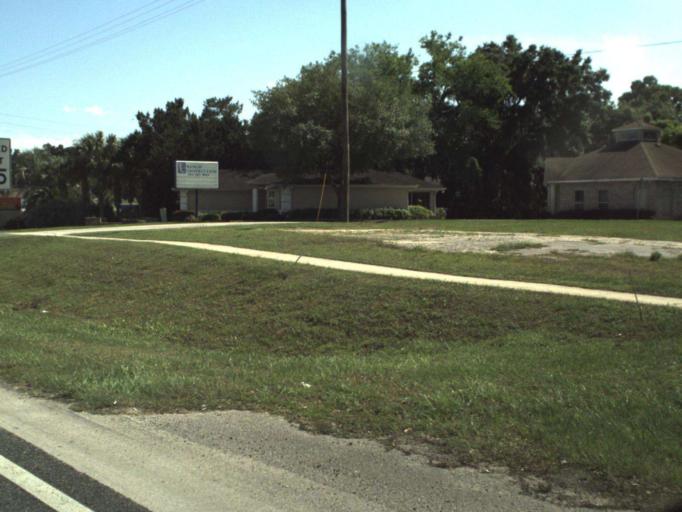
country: US
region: Florida
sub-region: Marion County
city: Belleview
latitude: 29.0653
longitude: -82.0682
